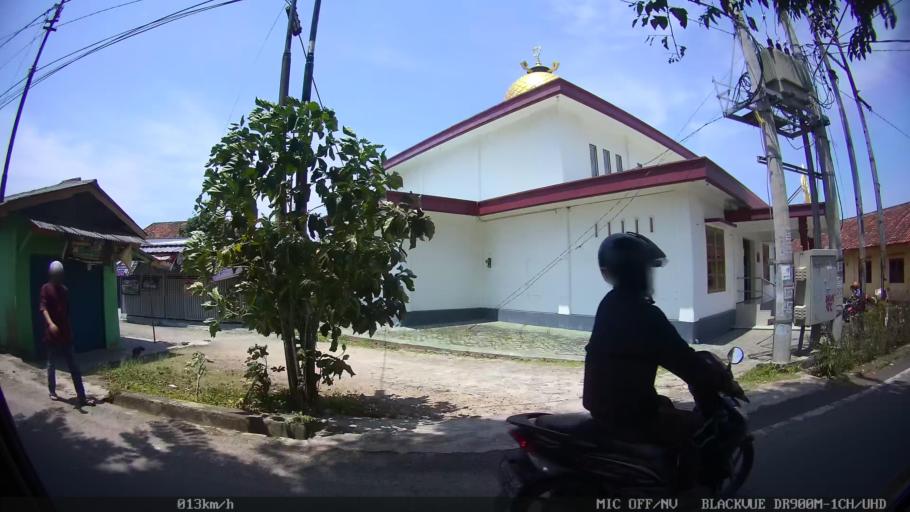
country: ID
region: Lampung
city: Kedaton
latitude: -5.4024
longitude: 105.2640
